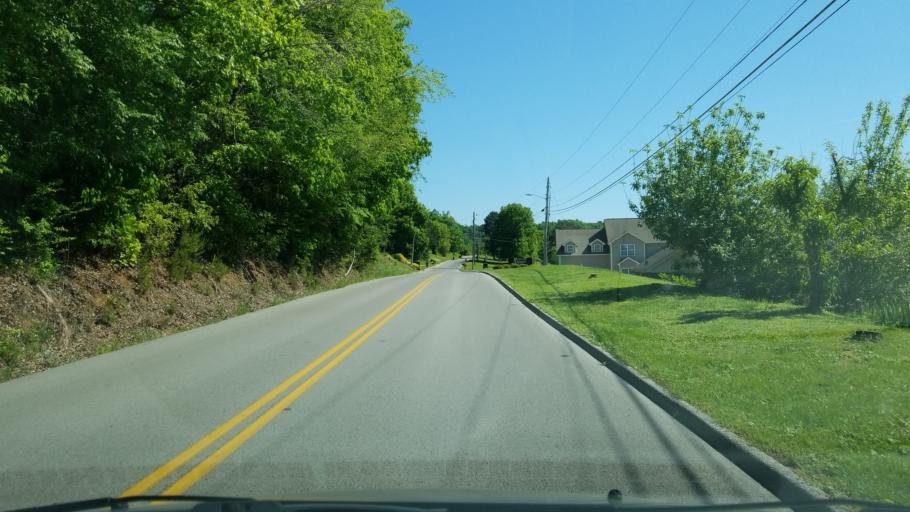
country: US
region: Tennessee
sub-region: Hamilton County
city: Red Bank
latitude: 35.1360
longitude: -85.3033
